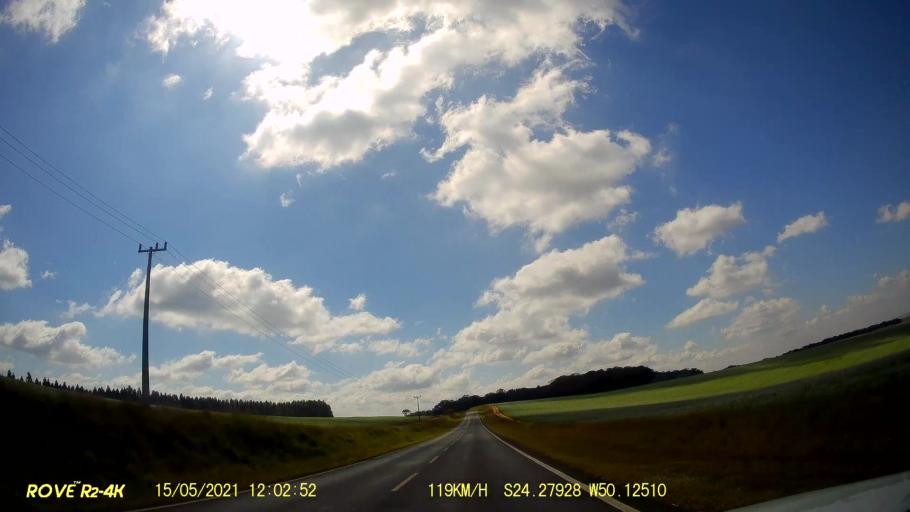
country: BR
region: Parana
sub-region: Pirai Do Sul
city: Pirai do Sul
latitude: -24.2794
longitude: -50.1250
